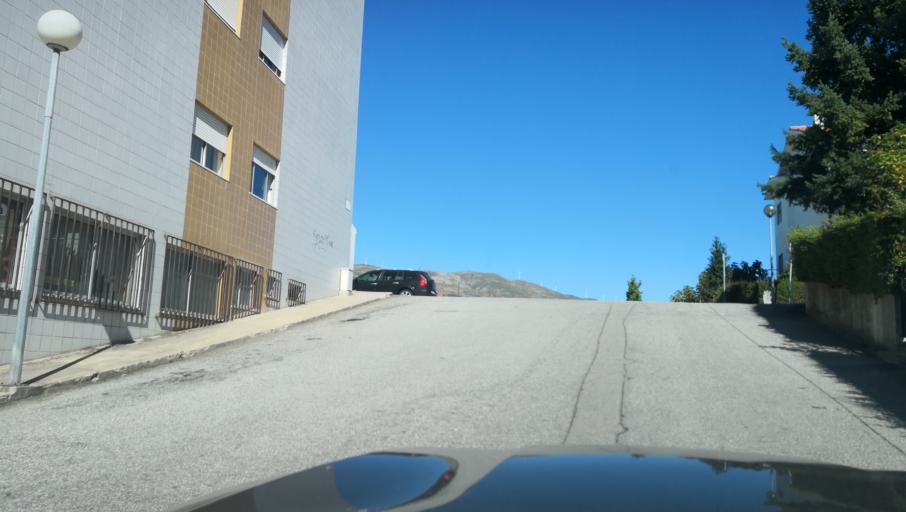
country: PT
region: Vila Real
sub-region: Vila Real
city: Vila Real
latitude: 41.3071
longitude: -7.7428
